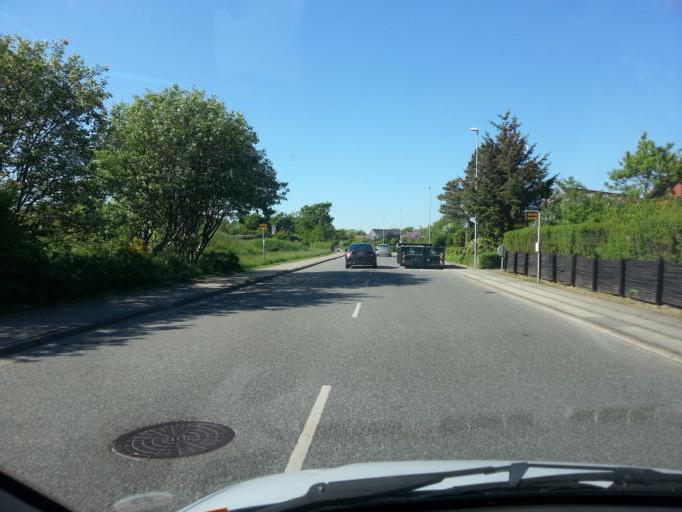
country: DK
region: South Denmark
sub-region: Fano Kommune
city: Nordby
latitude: 55.5321
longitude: 8.3483
